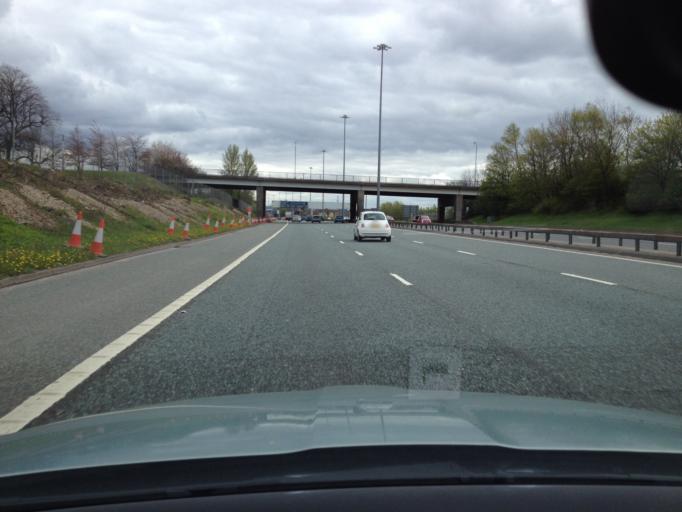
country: GB
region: Scotland
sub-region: North Lanarkshire
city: Stepps
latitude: 55.8641
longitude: -4.1235
